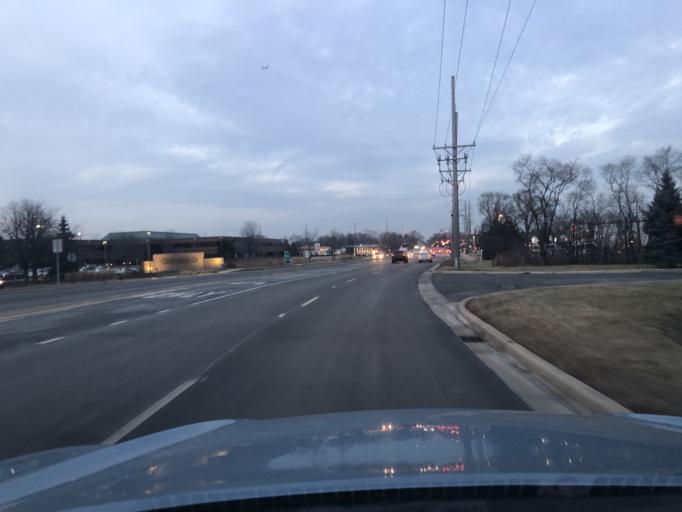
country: US
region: Illinois
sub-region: DuPage County
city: Itasca
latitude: 41.9893
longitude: -88.0031
